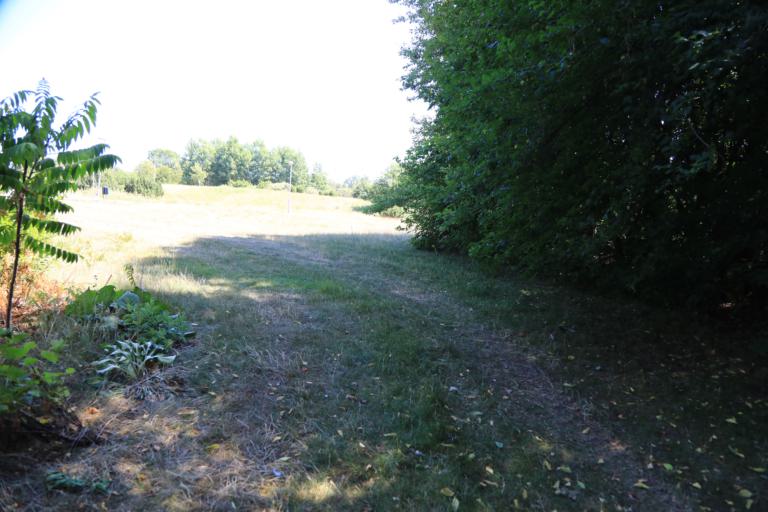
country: SE
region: Halland
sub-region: Halmstads Kommun
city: Fyllinge
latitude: 56.6639
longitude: 12.9107
